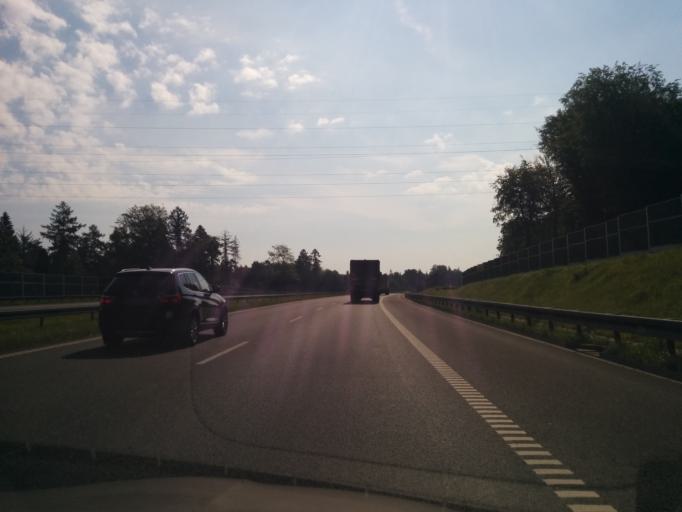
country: PL
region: Silesian Voivodeship
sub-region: Powiat tarnogorski
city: Tarnowskie Gory
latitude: 50.3876
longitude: 18.8429
